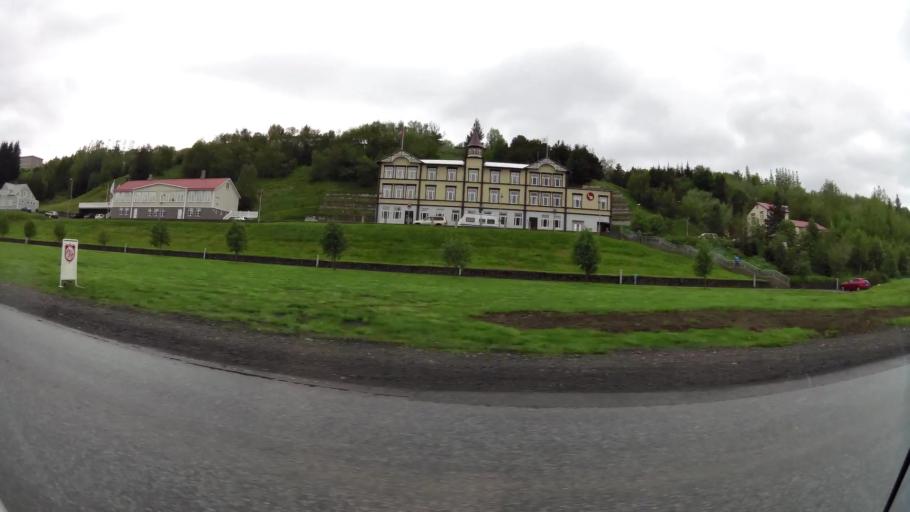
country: IS
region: Northeast
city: Akureyri
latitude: 65.6771
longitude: -18.0883
